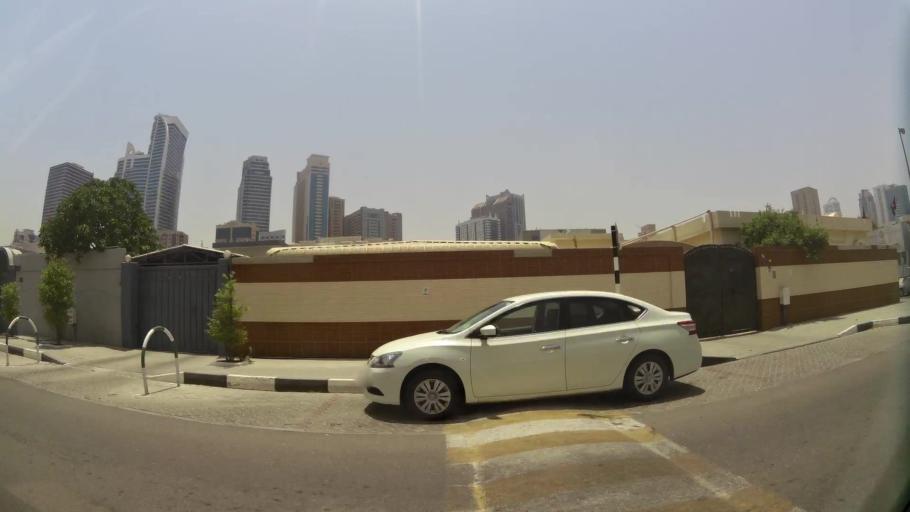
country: AE
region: Ash Shariqah
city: Sharjah
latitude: 25.3357
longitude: 55.3708
